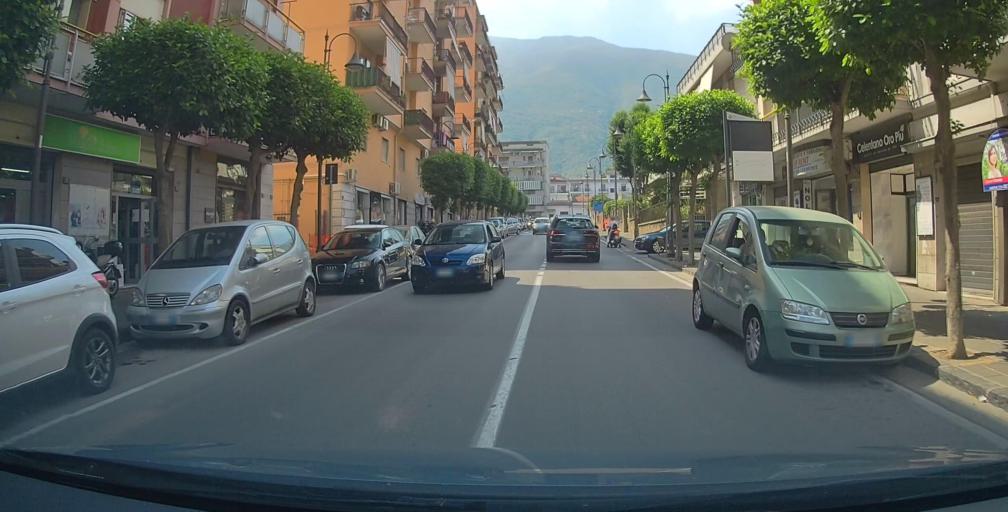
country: IT
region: Campania
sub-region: Provincia di Salerno
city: Nocera Inferiore
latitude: 40.7425
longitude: 14.6497
